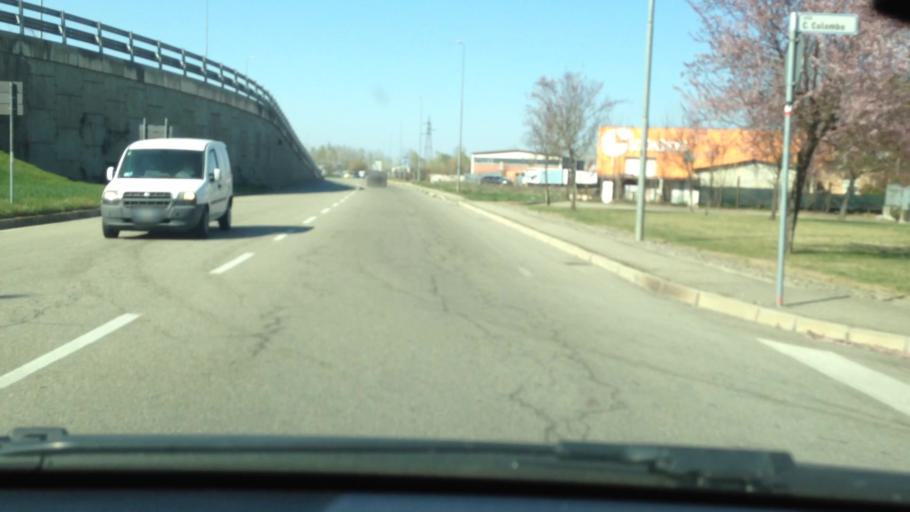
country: IT
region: Piedmont
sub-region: Provincia di Asti
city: Asti
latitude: 44.9165
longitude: 8.2290
